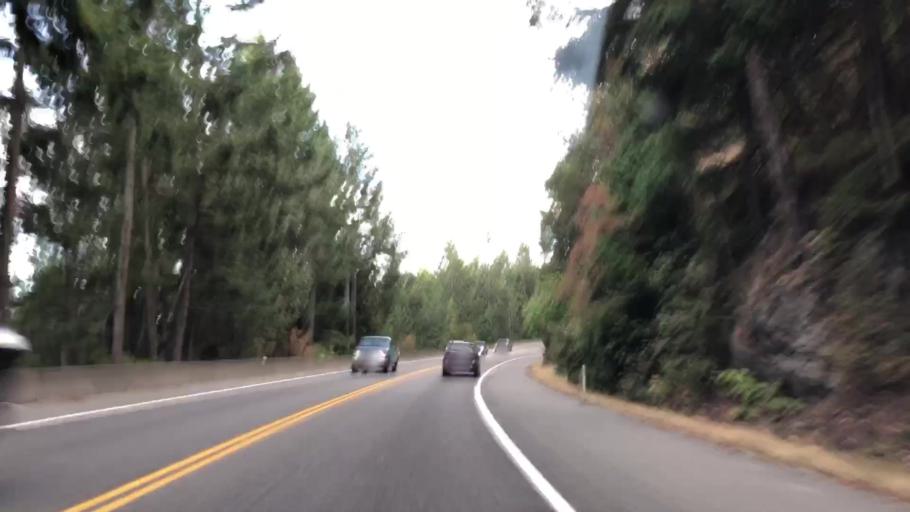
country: CA
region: British Columbia
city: Langford
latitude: 48.5764
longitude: -123.5273
